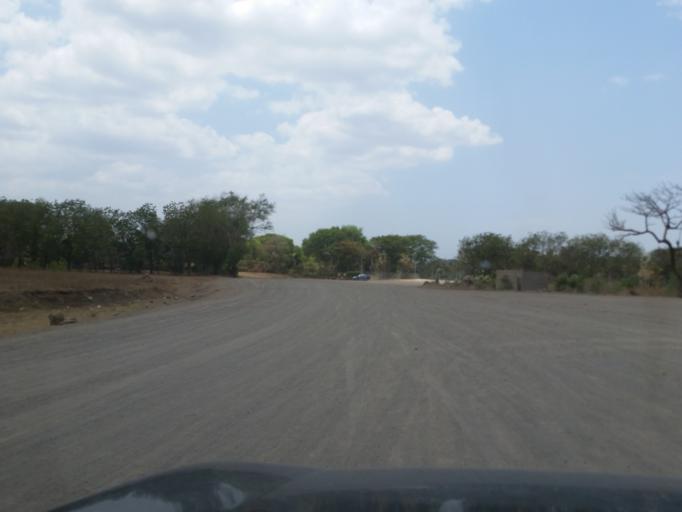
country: NI
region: Managua
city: Managua
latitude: 12.1348
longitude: -86.1617
